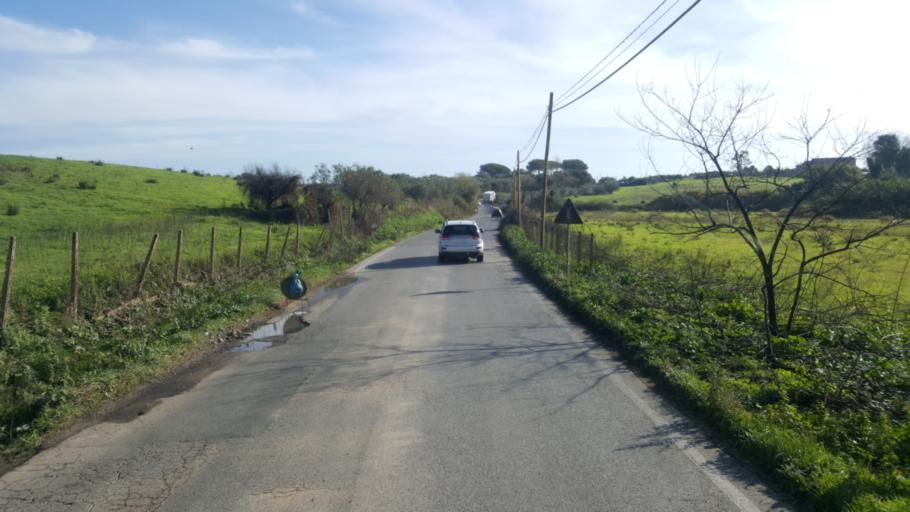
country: IT
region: Latium
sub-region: Citta metropolitana di Roma Capitale
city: Mantiglia di Ardea
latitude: 41.6839
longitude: 12.6144
